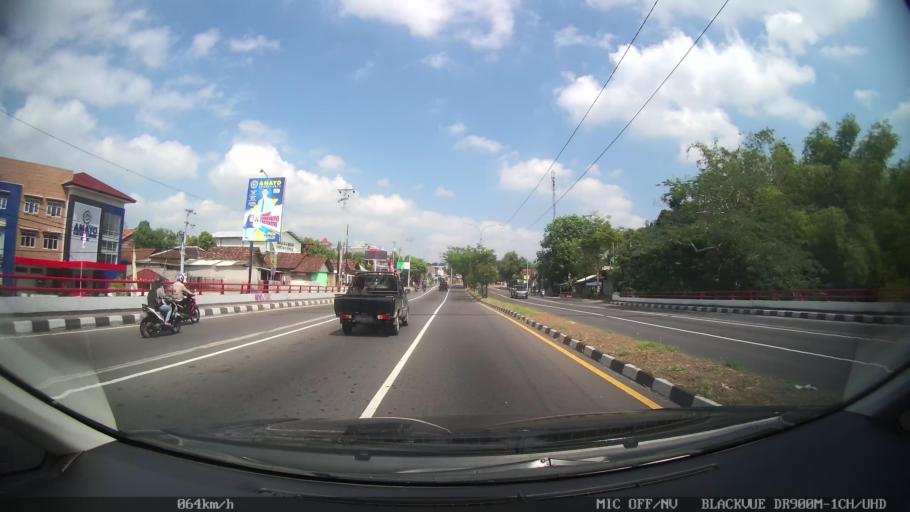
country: ID
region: Daerah Istimewa Yogyakarta
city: Kasihan
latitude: -7.8256
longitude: 110.3367
